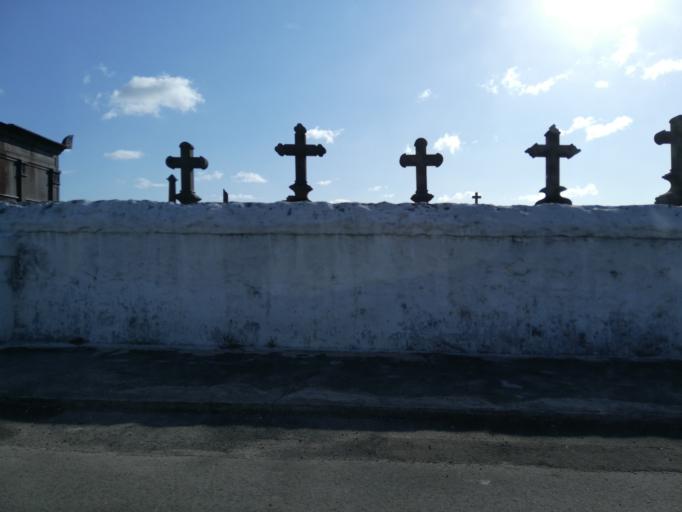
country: MU
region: Port Louis
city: Port Louis
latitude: -20.1605
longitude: 57.4871
